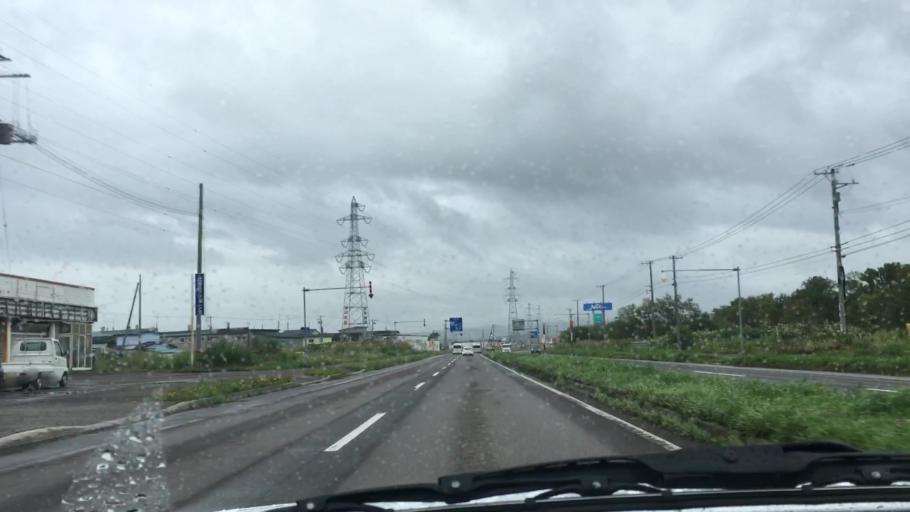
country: JP
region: Hokkaido
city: Nanae
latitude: 42.2559
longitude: 140.2810
